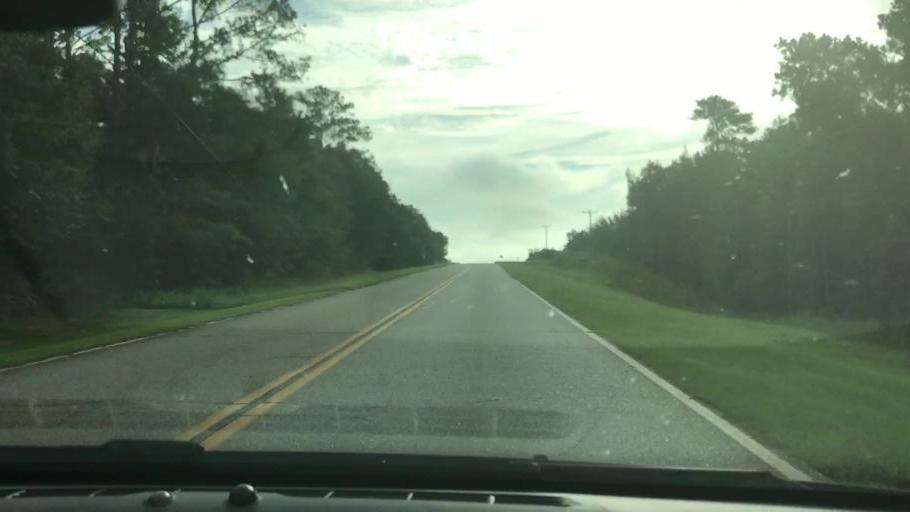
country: US
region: Georgia
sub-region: Quitman County
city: Georgetown
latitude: 31.8950
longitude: -85.0616
